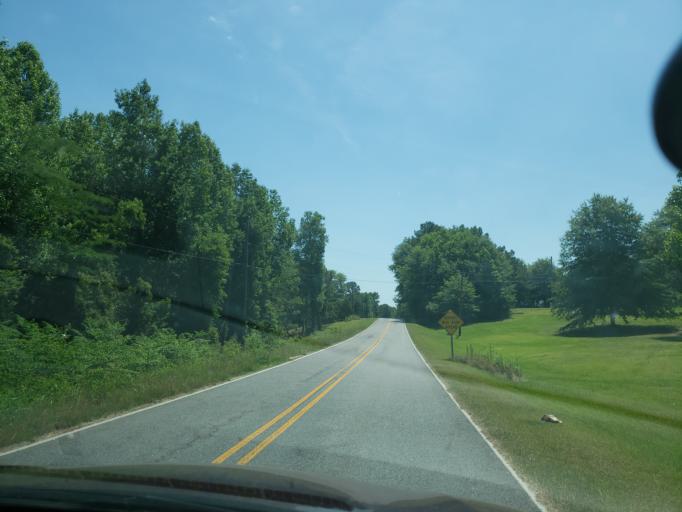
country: US
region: Alabama
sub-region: Elmore County
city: Tallassee
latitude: 32.5804
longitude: -85.8539
